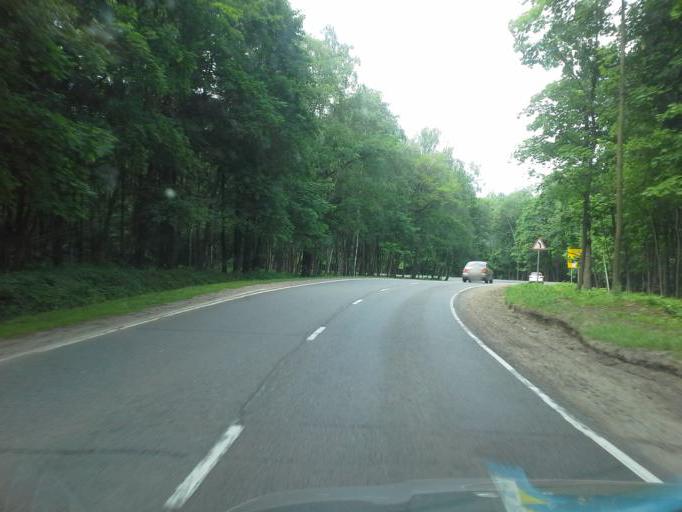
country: RU
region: Moskovskaya
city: Odintsovo
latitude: 55.6930
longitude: 37.2377
